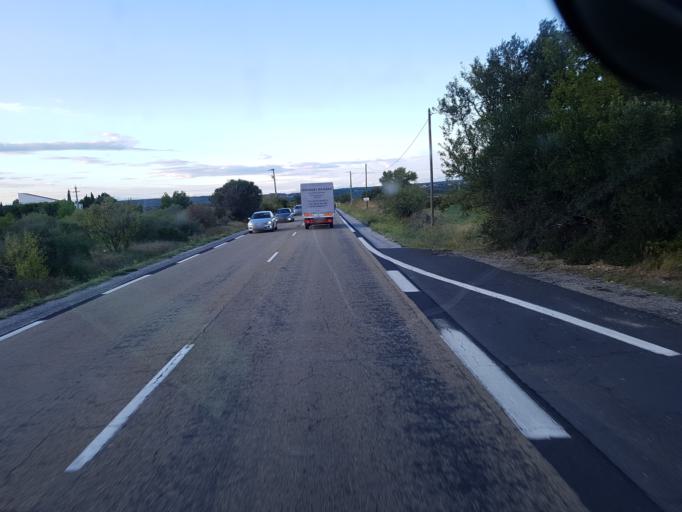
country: FR
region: Languedoc-Roussillon
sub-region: Departement de l'Aude
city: Leucate
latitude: 42.9460
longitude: 2.9884
